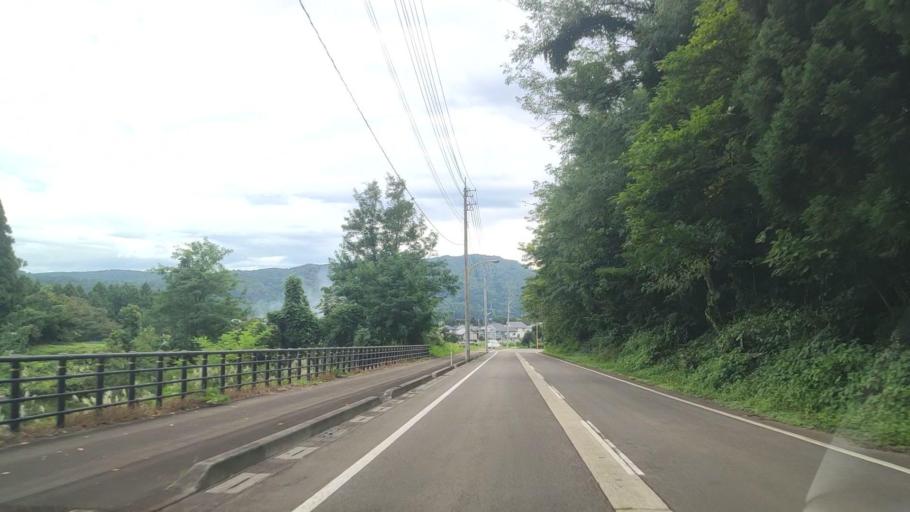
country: JP
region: Niigata
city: Arai
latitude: 37.0124
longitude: 138.2546
